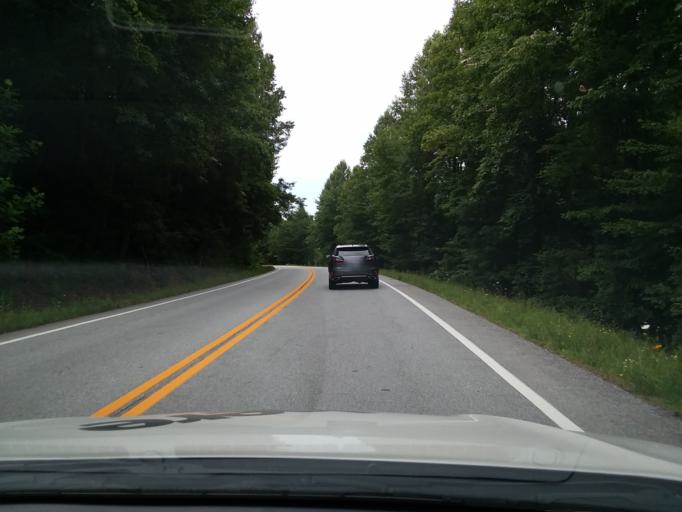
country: US
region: Georgia
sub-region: Rabun County
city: Clayton
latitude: 34.8264
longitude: -83.3222
